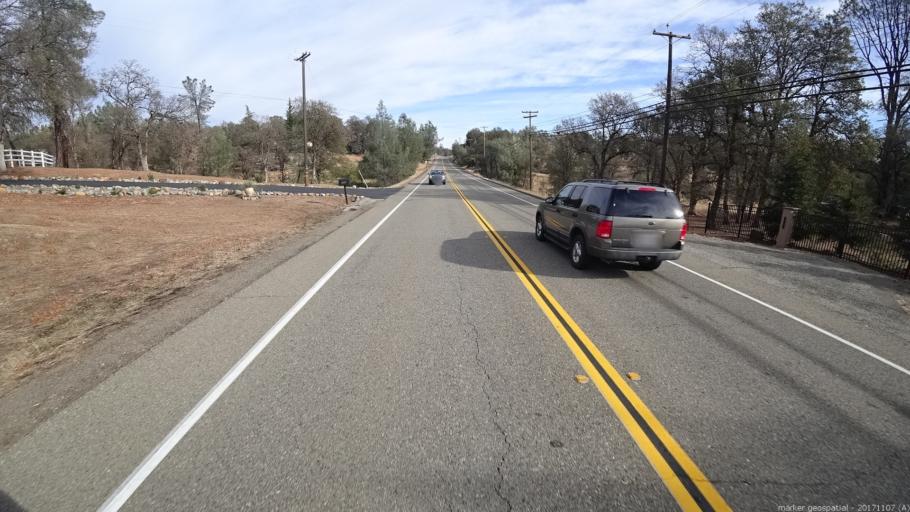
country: US
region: California
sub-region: Shasta County
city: Shasta
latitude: 40.5428
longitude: -122.4673
